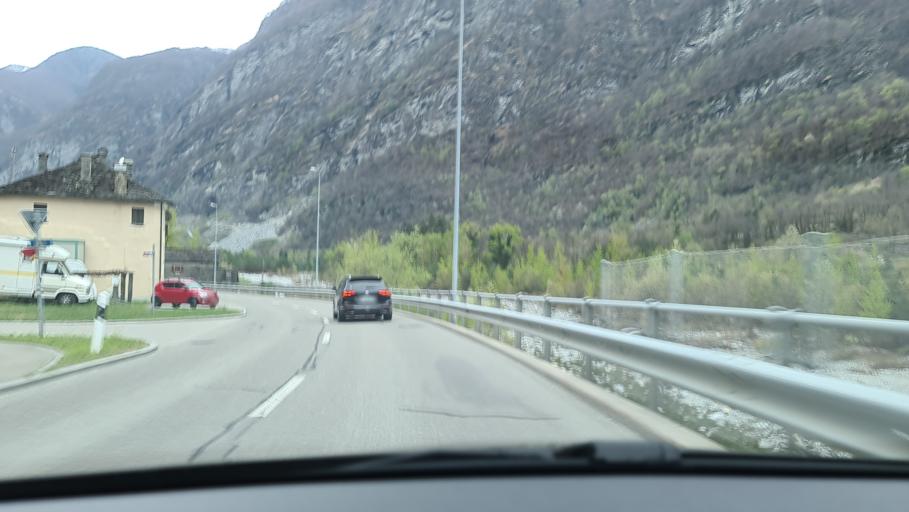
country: CH
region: Ticino
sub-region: Vallemaggia District
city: Cevio
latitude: 46.3086
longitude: 8.6103
